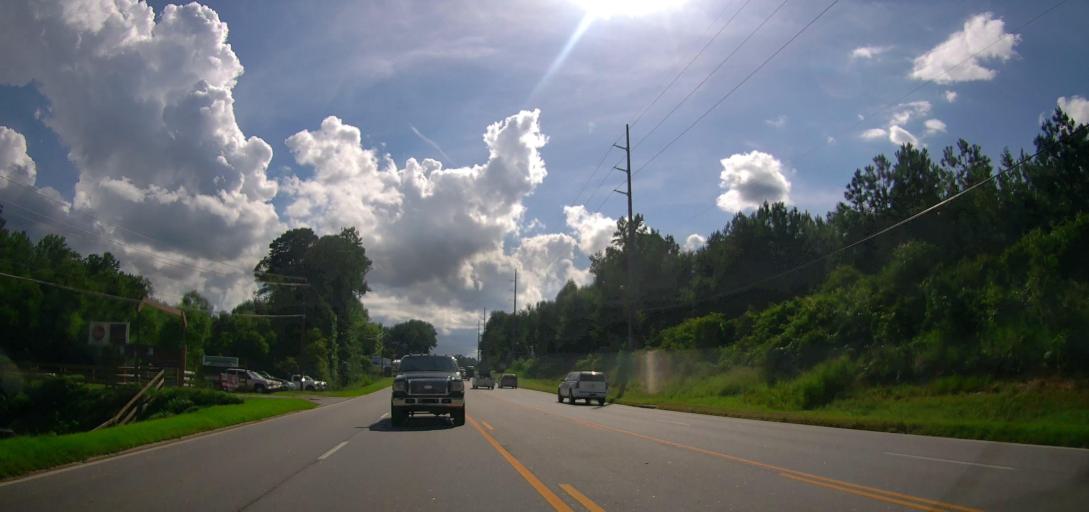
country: US
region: Alabama
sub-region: Russell County
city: Ladonia
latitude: 32.4737
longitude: -85.0448
